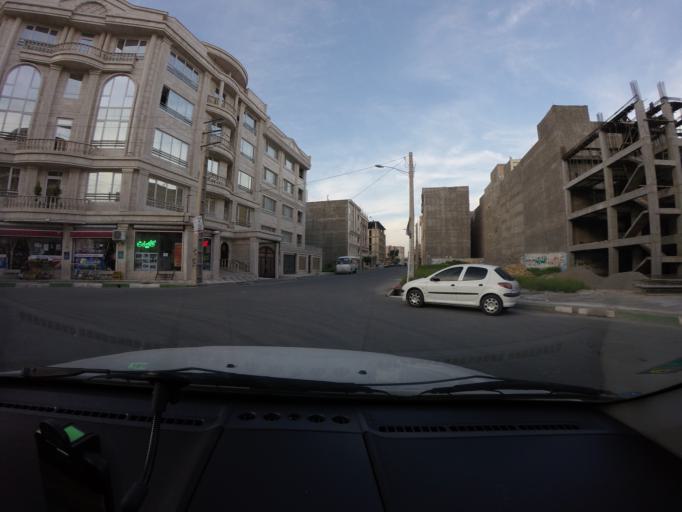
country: IR
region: Tehran
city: Eslamshahr
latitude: 35.5498
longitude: 51.2334
